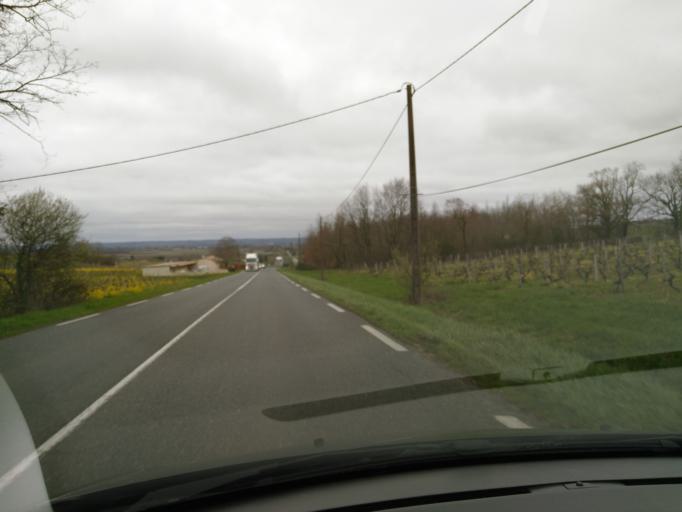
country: FR
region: Aquitaine
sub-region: Departement de la Dordogne
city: Monbazillac
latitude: 44.7945
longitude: 0.5240
